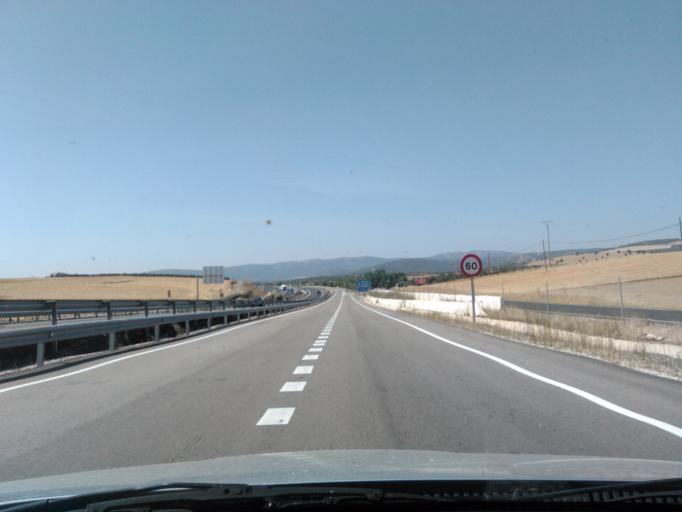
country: ES
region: Castille-La Mancha
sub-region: Provincia de Ciudad Real
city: Viso del Marques
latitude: 38.5024
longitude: -3.5011
